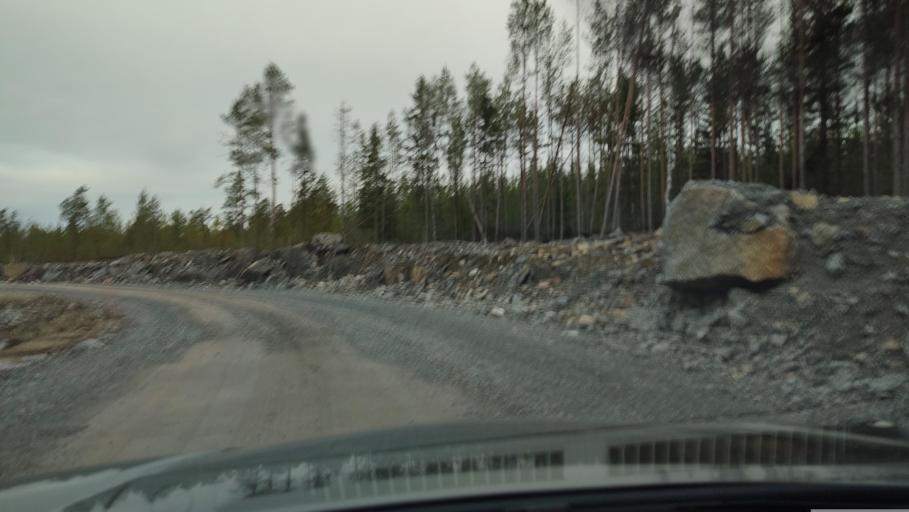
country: FI
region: Southern Ostrobothnia
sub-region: Suupohja
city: Karijoki
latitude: 62.1999
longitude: 21.5527
